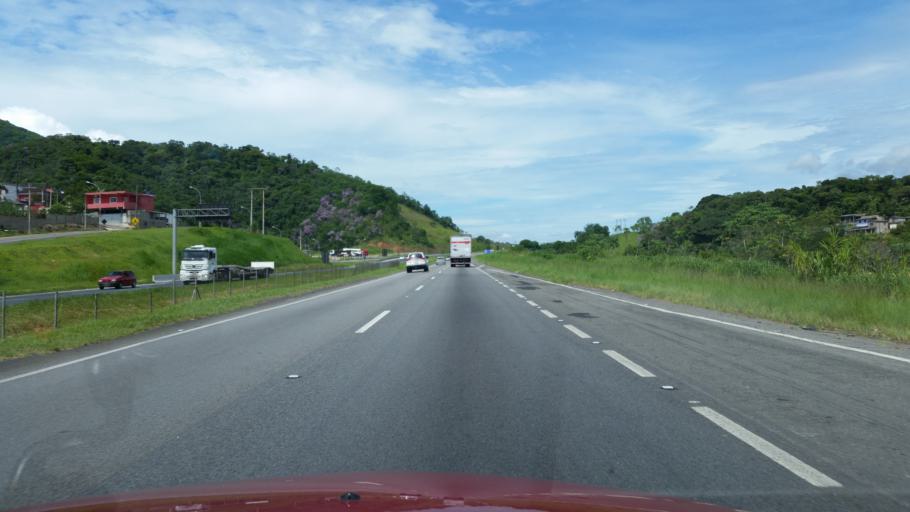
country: BR
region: Sao Paulo
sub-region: Miracatu
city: Miracatu
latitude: -24.2900
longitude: -47.4644
